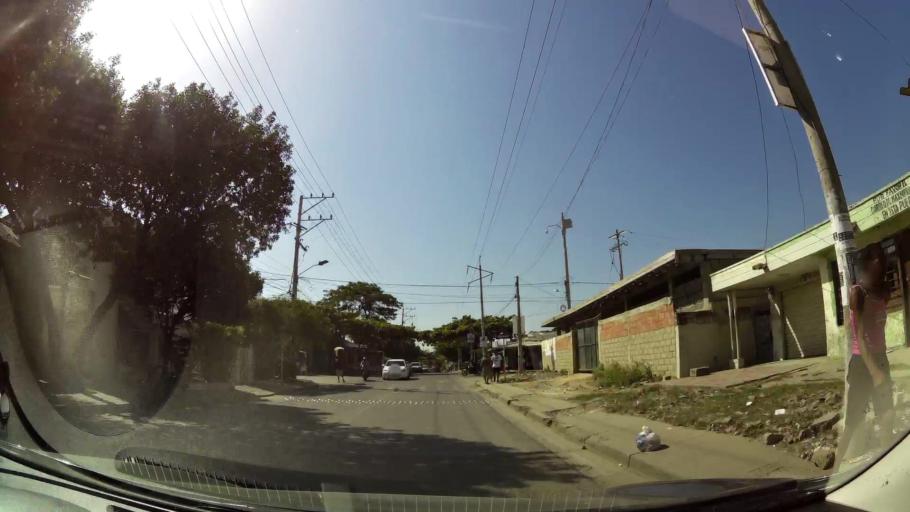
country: CO
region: Bolivar
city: Cartagena
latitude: 10.3849
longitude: -75.4658
